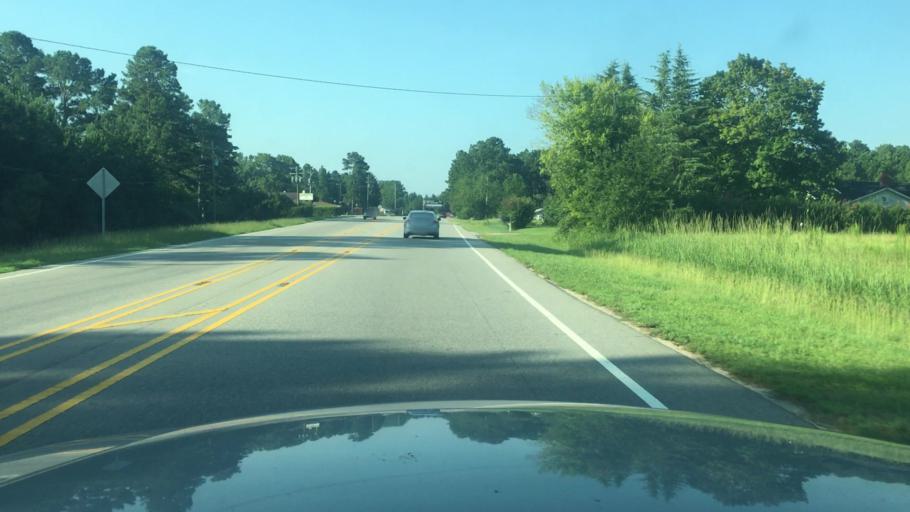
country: US
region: North Carolina
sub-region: Cumberland County
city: Eastover
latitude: 35.1861
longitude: -78.8525
